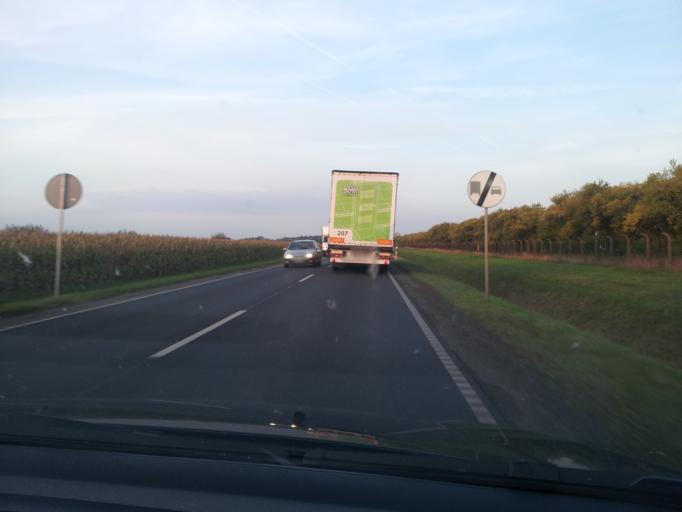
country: PL
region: Kujawsko-Pomorskie
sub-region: Powiat inowroclawski
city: Wierzchoslawice
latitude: 52.8315
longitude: 18.3135
